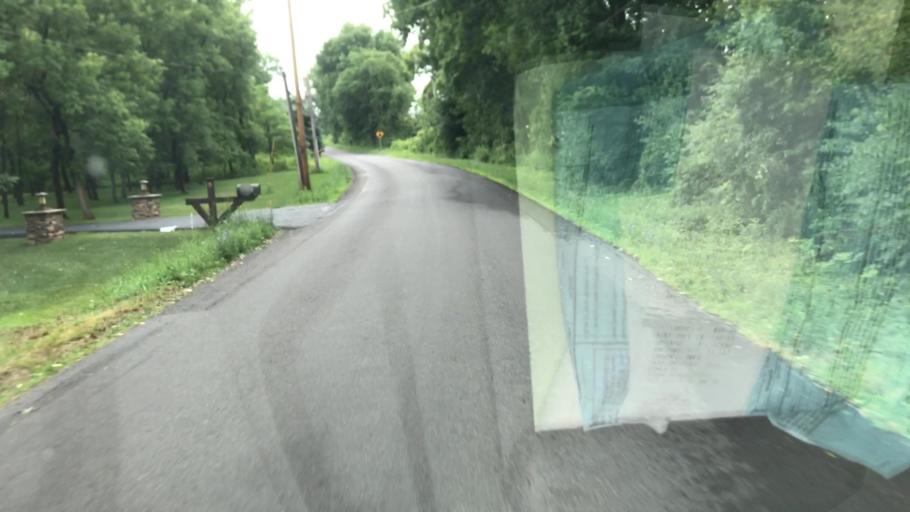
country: US
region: New York
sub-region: Onondaga County
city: Manlius
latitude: 42.9819
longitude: -75.9845
